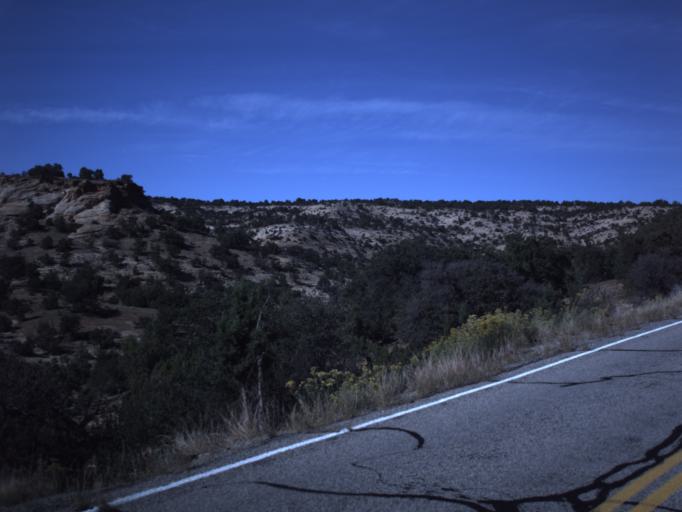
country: US
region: Utah
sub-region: San Juan County
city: Monticello
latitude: 37.9892
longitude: -109.4950
